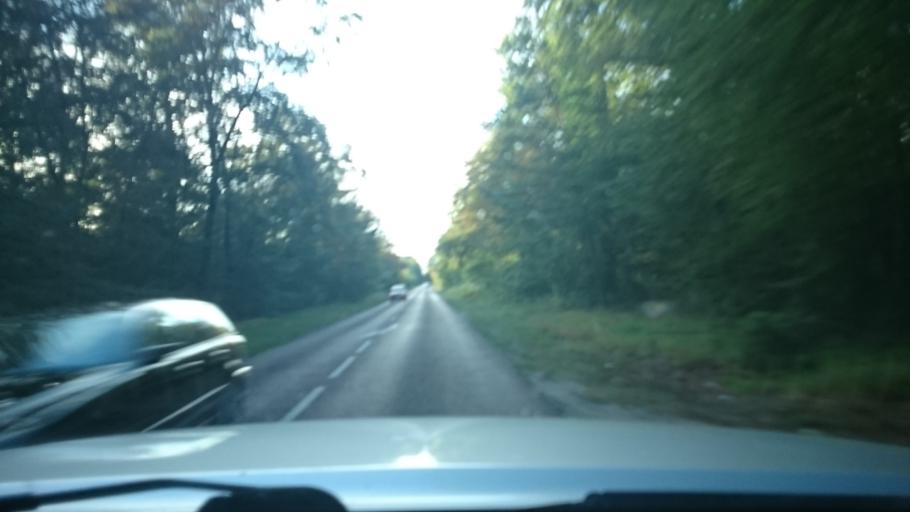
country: FR
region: Ile-de-France
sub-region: Departement de Seine-et-Marne
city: Thomery
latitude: 48.3982
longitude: 2.7626
